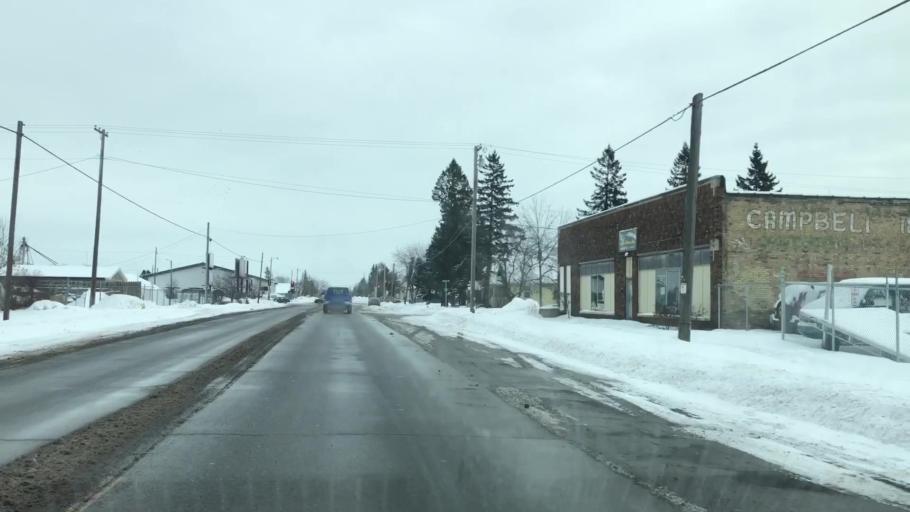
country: US
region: Wisconsin
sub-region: Douglas County
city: Superior
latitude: 46.7279
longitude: -92.1001
